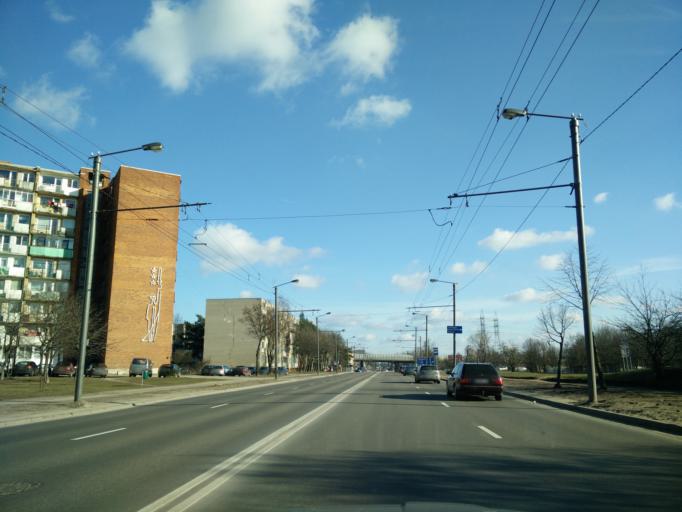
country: LT
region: Kauno apskritis
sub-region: Kauno rajonas
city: Akademija (Kaunas)
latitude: 54.9177
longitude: 23.8324
